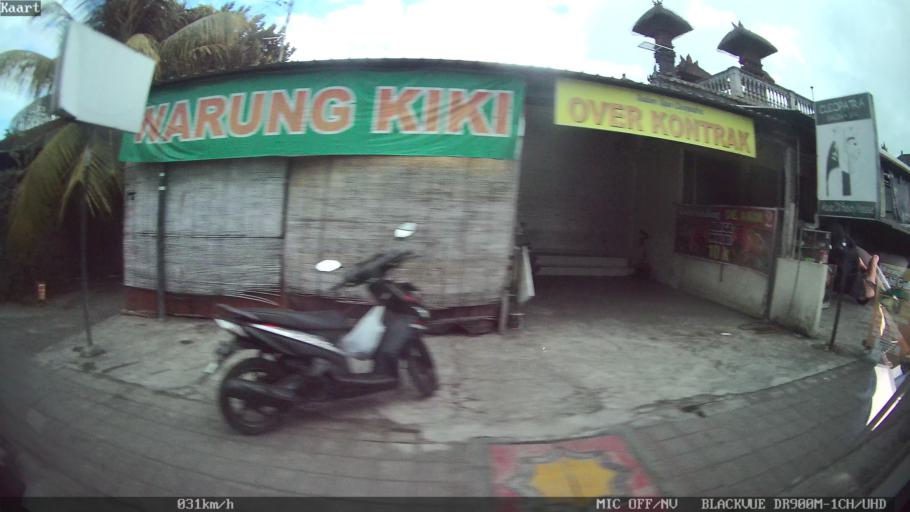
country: ID
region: Bali
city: Banjar Pekenjelodan
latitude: -8.5815
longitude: 115.1809
